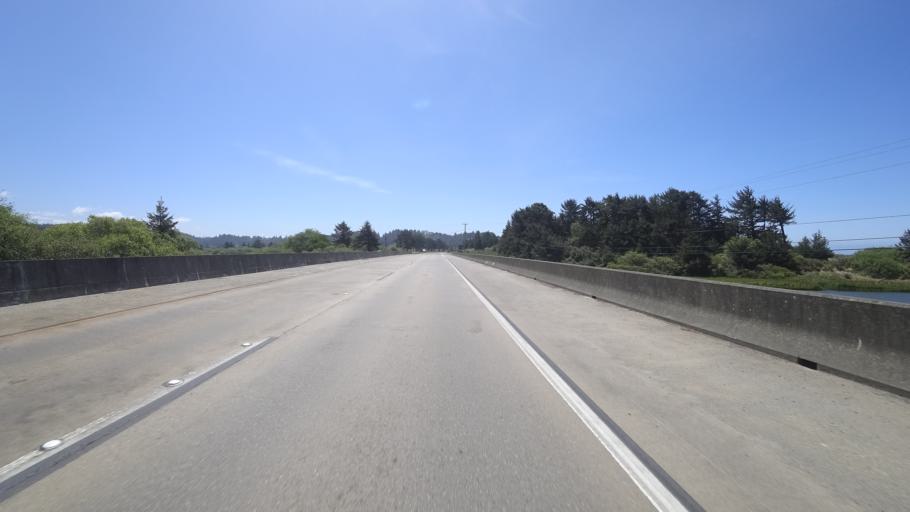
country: US
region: California
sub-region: Humboldt County
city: Westhaven-Moonstone
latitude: 41.0211
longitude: -124.1072
